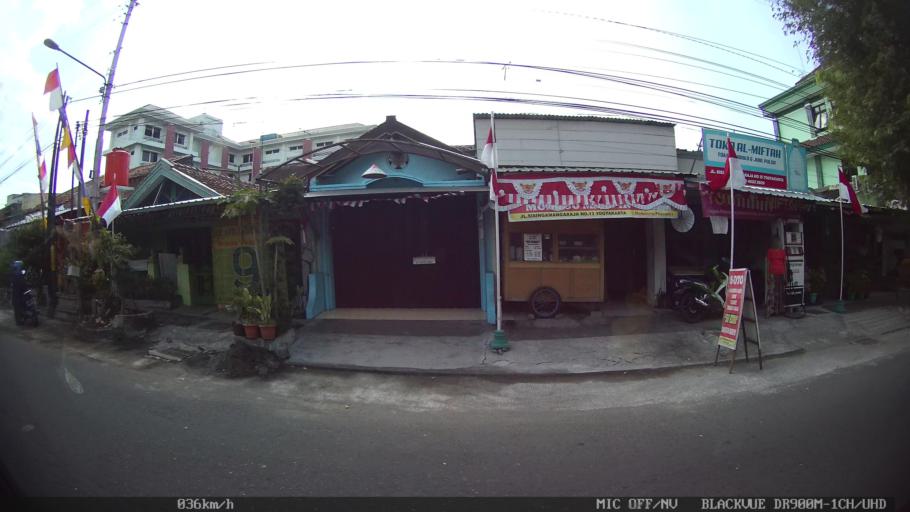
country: ID
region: Daerah Istimewa Yogyakarta
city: Yogyakarta
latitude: -7.8167
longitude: 110.3732
